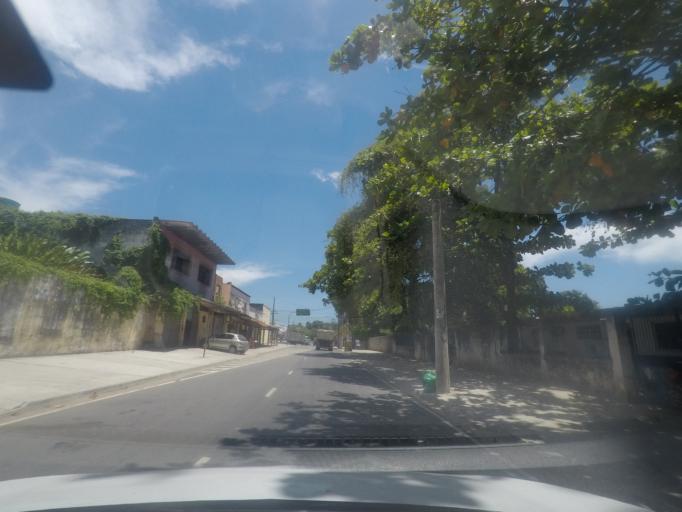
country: BR
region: Rio de Janeiro
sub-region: Itaguai
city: Itaguai
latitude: -22.9253
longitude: -43.6910
